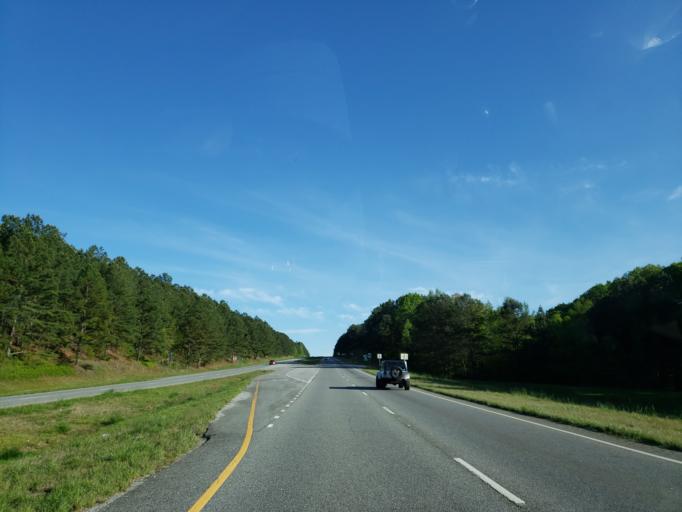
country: US
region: Georgia
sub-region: Polk County
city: Rockmart
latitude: 33.9534
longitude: -84.9835
